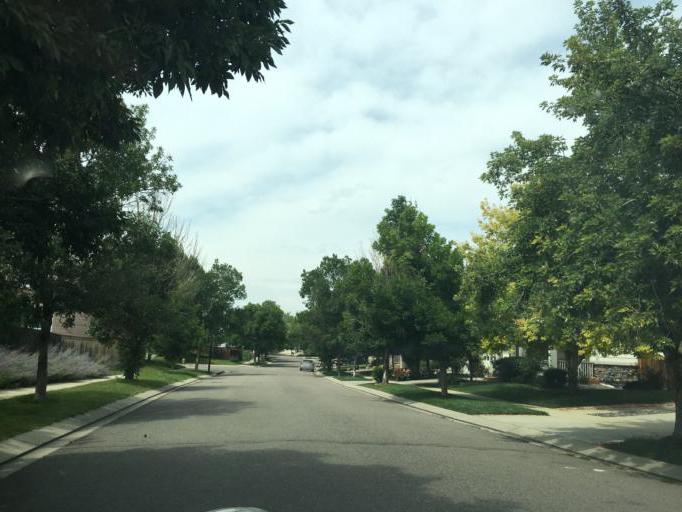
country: US
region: Colorado
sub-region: Adams County
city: Aurora
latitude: 39.7278
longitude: -104.8070
